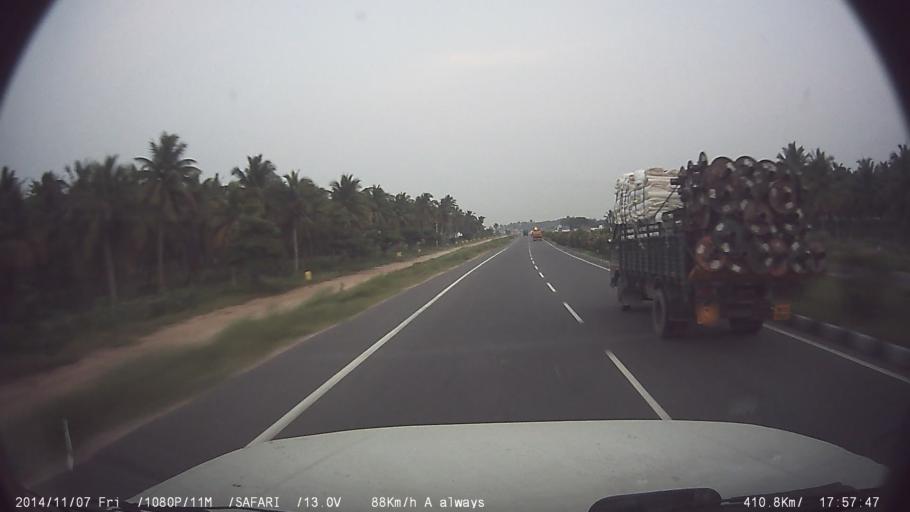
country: IN
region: Tamil Nadu
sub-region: Erode
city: Perundurai
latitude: 11.3417
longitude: 77.6327
